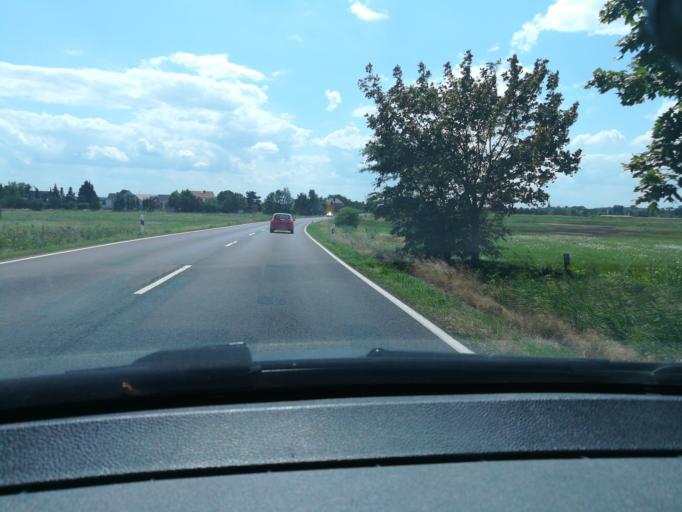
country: DE
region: Saxony-Anhalt
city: Zielitz
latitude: 52.2983
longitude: 11.6943
